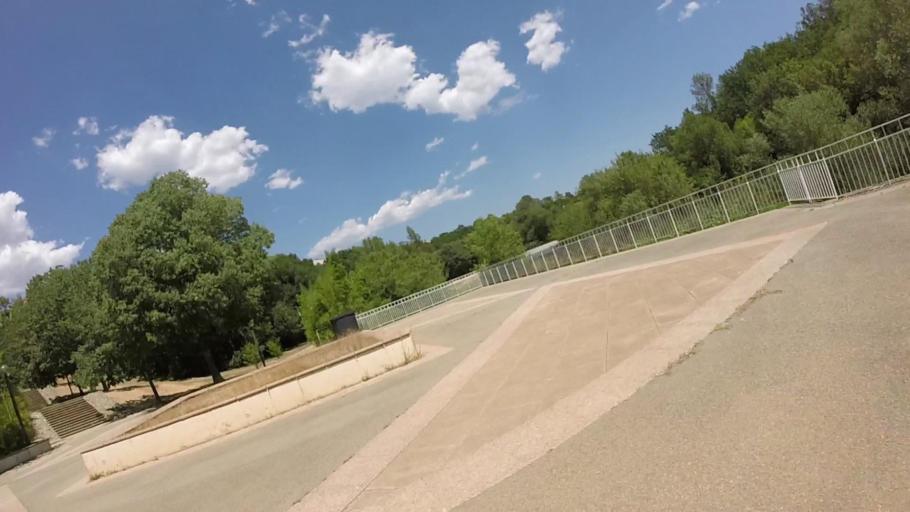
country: FR
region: Provence-Alpes-Cote d'Azur
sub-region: Departement des Alpes-Maritimes
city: Vallauris
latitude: 43.6200
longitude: 7.0489
